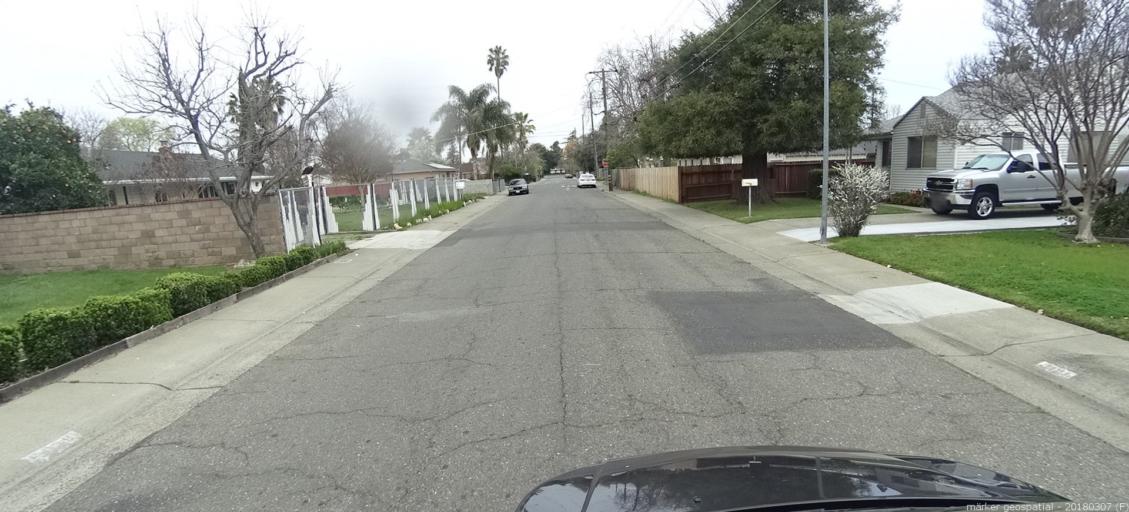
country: US
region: California
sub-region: Sacramento County
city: Parkway
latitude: 38.5295
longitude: -121.4616
